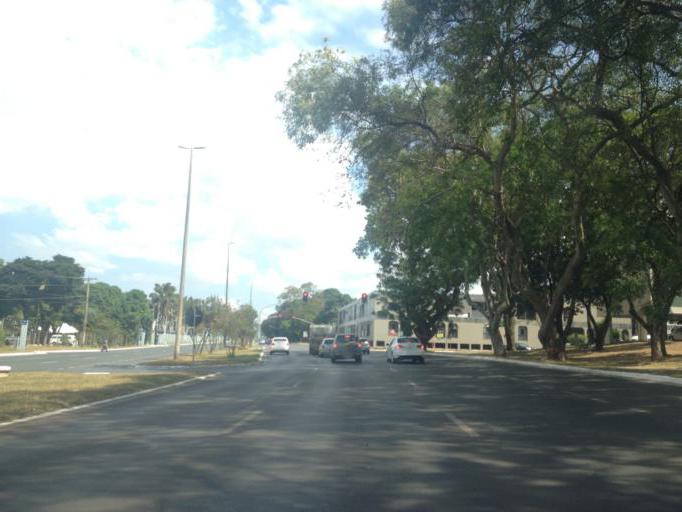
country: BR
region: Federal District
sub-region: Brasilia
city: Brasilia
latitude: -15.8353
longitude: -47.9152
